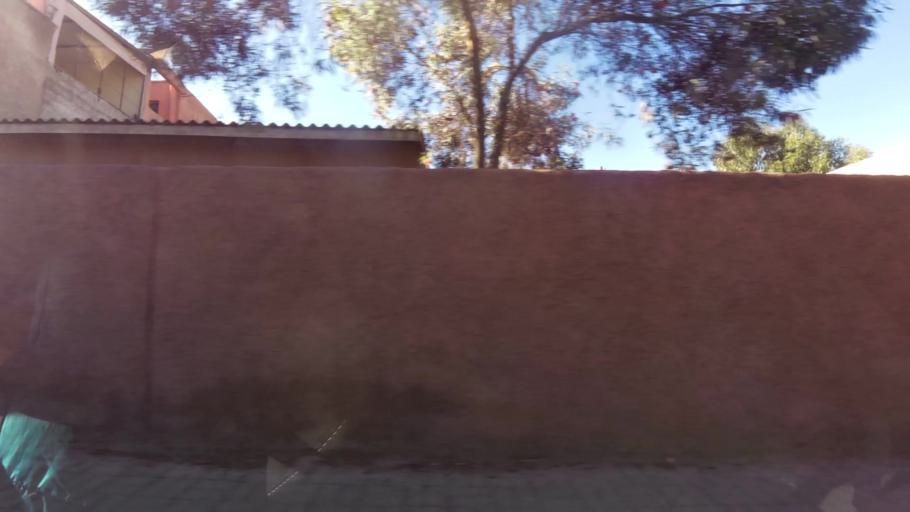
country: MA
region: Marrakech-Tensift-Al Haouz
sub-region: Marrakech
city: Marrakesh
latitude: 31.5977
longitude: -8.0305
